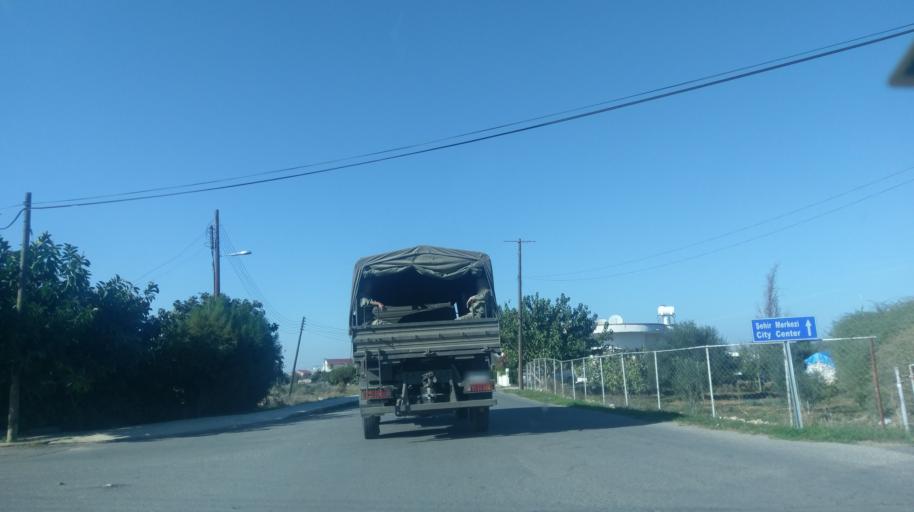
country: CY
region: Ammochostos
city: Famagusta
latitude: 35.1006
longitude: 33.9489
